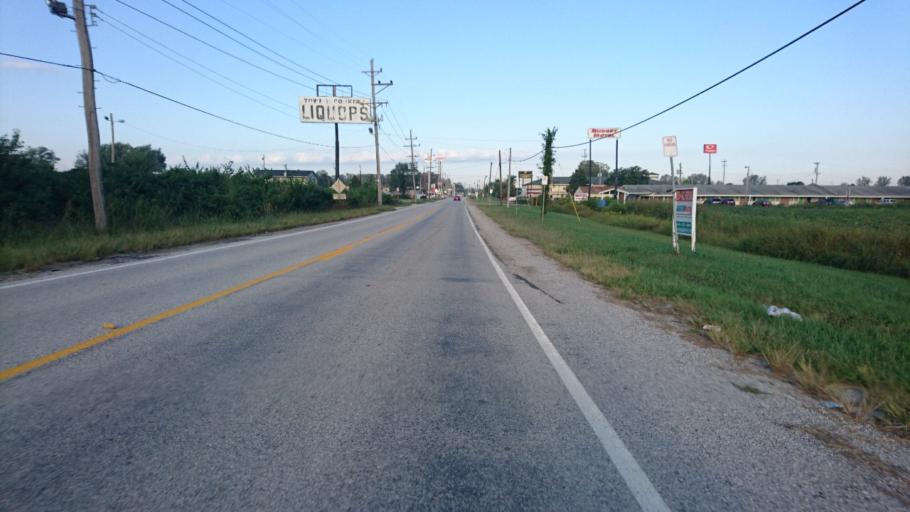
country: US
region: Illinois
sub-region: Madison County
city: Mitchell
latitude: 38.7620
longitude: -90.1186
